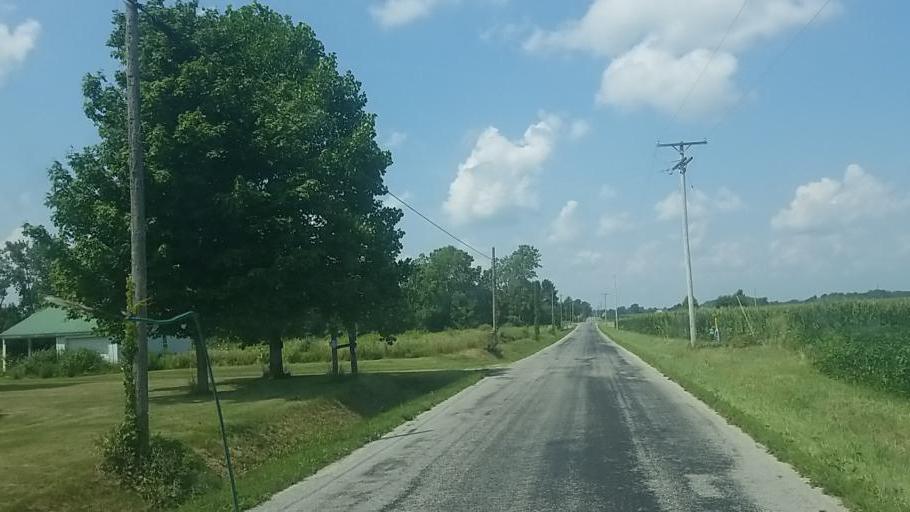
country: US
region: Ohio
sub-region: Crawford County
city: Crestline
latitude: 40.7988
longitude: -82.7139
